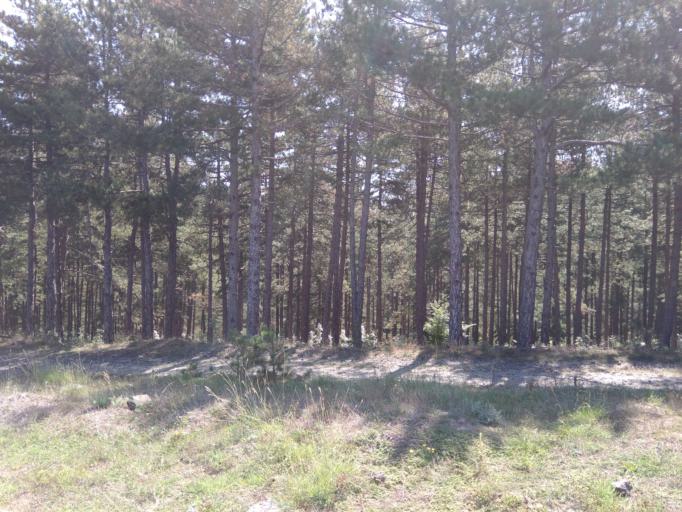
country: BG
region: Kurdzhali
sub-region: Obshtina Kurdzhali
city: Kurdzhali
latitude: 41.6312
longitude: 25.4520
